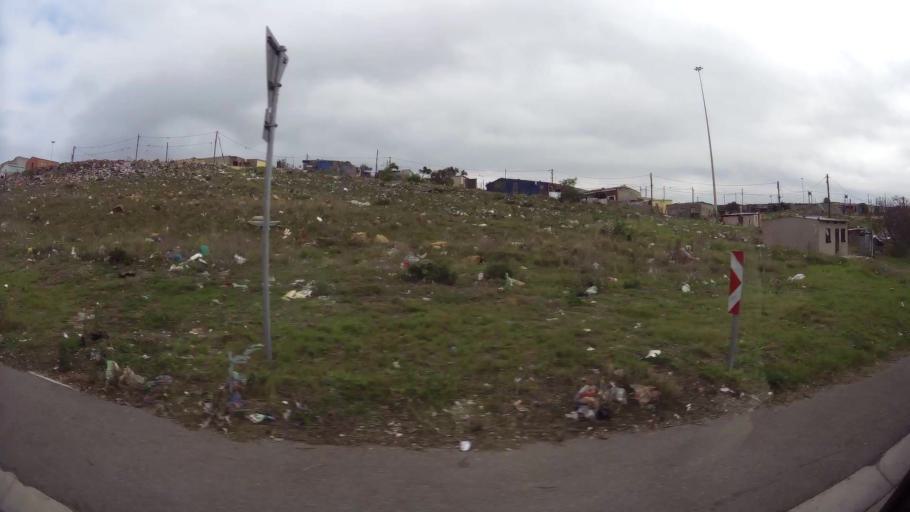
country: ZA
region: Eastern Cape
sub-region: Nelson Mandela Bay Metropolitan Municipality
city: Port Elizabeth
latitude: -33.9121
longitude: 25.5387
